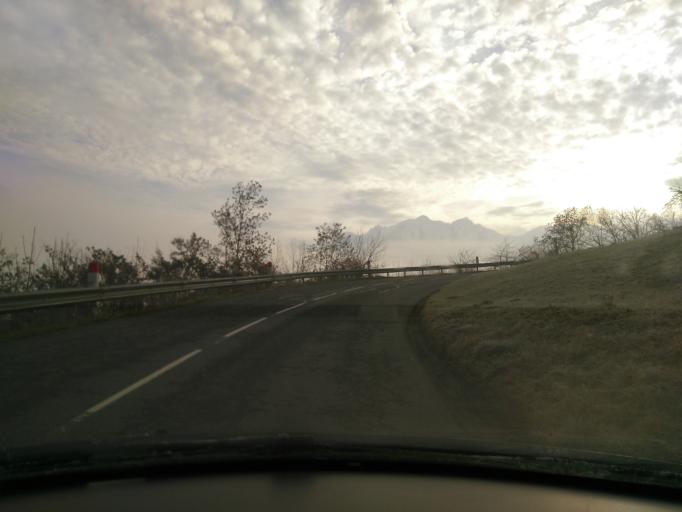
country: FR
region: Rhone-Alpes
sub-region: Departement de la Haute-Savoie
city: Sallanches
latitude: 45.9347
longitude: 6.6265
